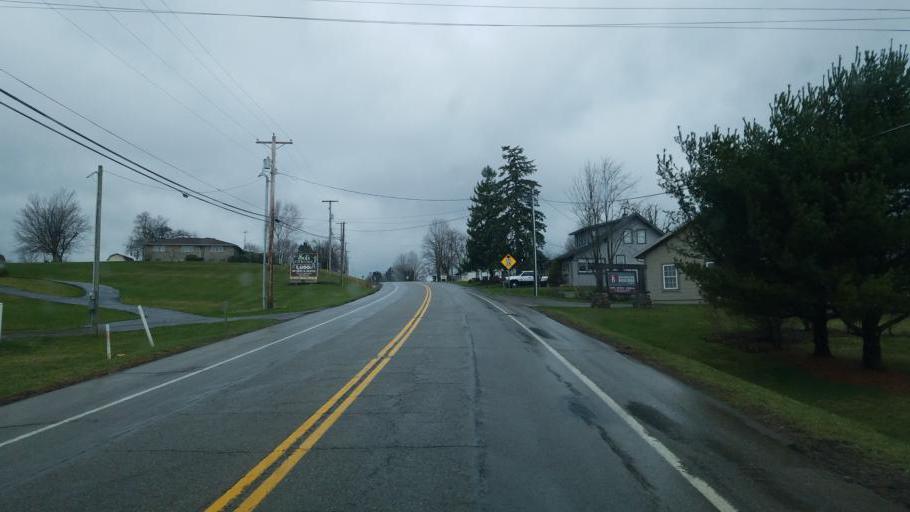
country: US
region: Ohio
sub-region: Holmes County
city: Millersburg
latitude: 40.5669
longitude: -81.7874
